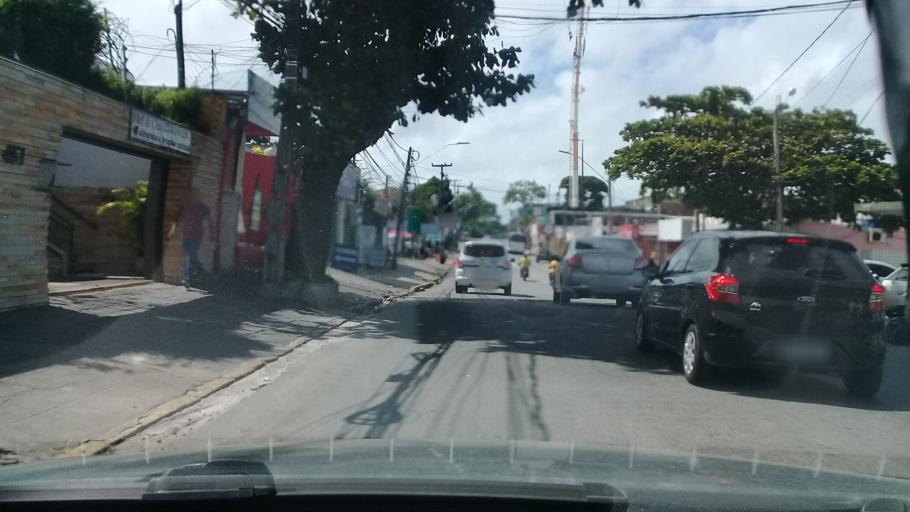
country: BR
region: Pernambuco
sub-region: Jaboatao Dos Guararapes
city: Jaboatao
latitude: -8.1648
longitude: -34.9192
